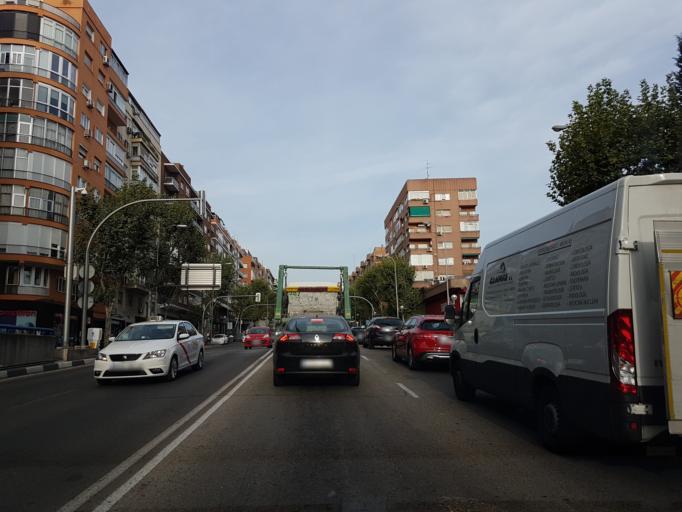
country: ES
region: Madrid
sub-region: Provincia de Madrid
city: Retiro
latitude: 40.4070
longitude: -3.6719
